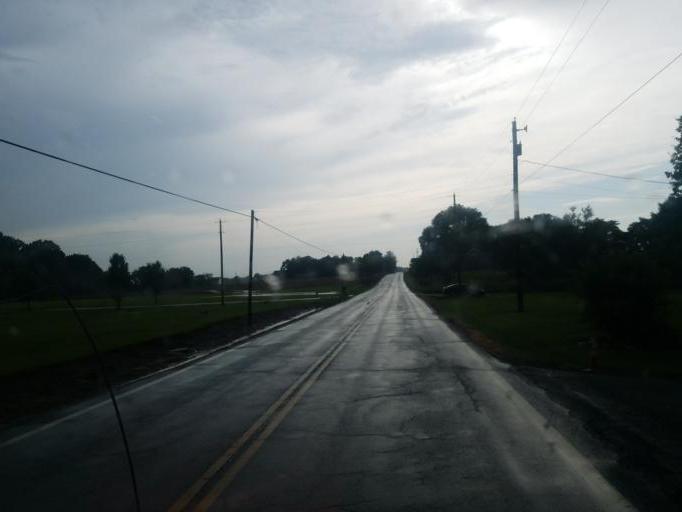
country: US
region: Ohio
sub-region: Wayne County
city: Creston
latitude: 40.9445
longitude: -81.9523
